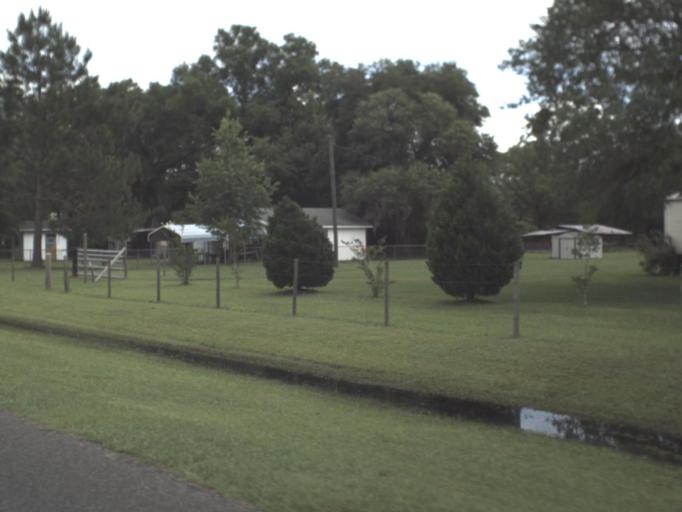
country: US
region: Florida
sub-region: Nassau County
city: Hilliard
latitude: 30.7259
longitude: -81.9419
